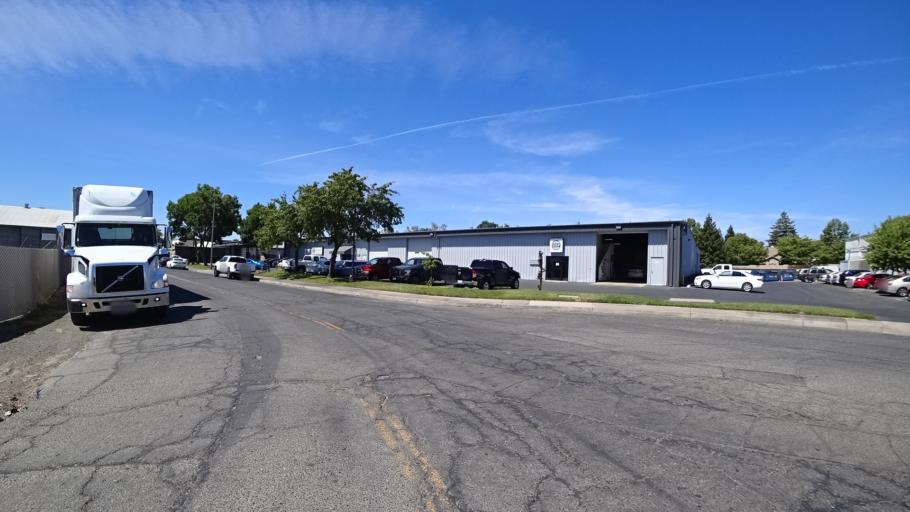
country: US
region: California
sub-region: Sacramento County
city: Parkway
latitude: 38.5091
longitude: -121.5045
